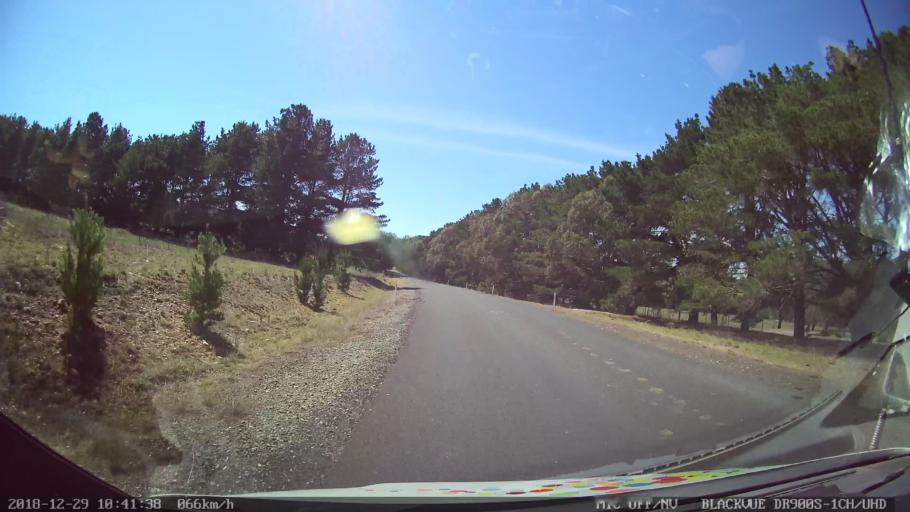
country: AU
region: New South Wales
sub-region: Palerang
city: Bungendore
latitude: -35.0274
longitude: 149.5220
